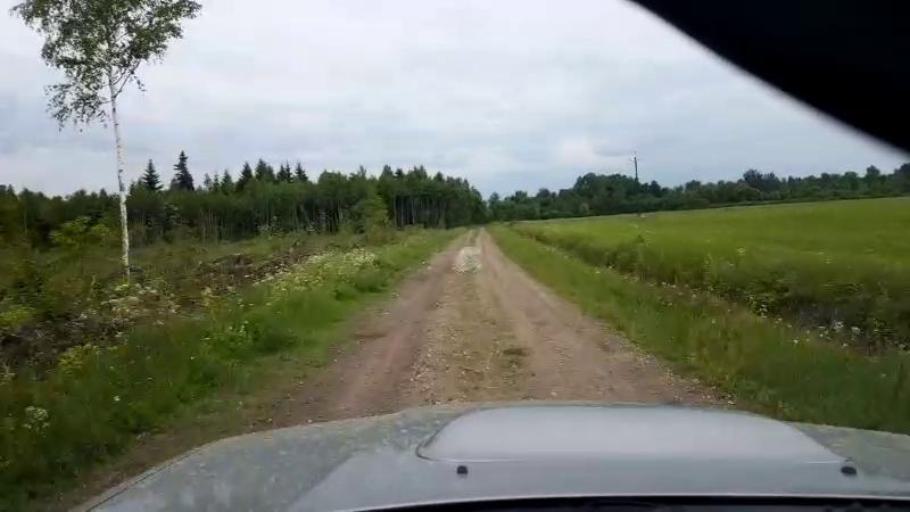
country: EE
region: Paernumaa
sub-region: Tootsi vald
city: Tootsi
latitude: 58.5977
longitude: 24.6629
